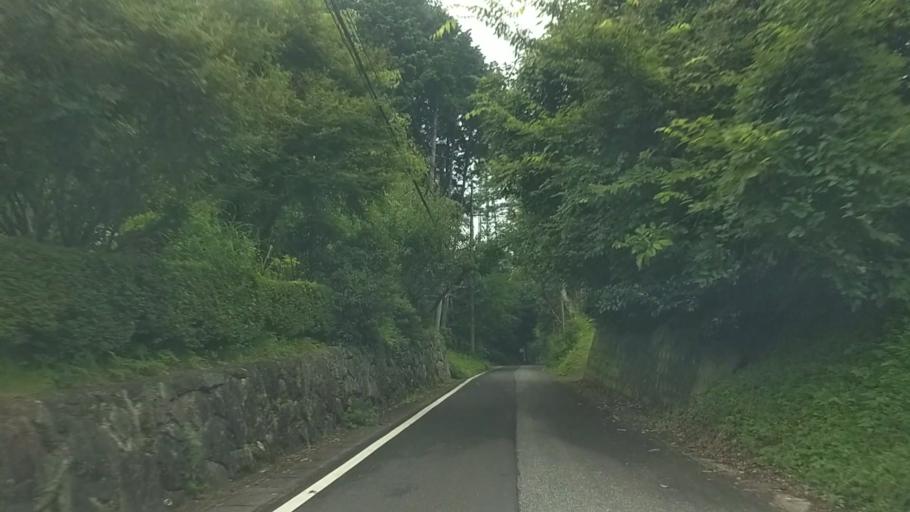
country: JP
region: Chiba
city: Kawaguchi
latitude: 35.2524
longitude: 140.0664
